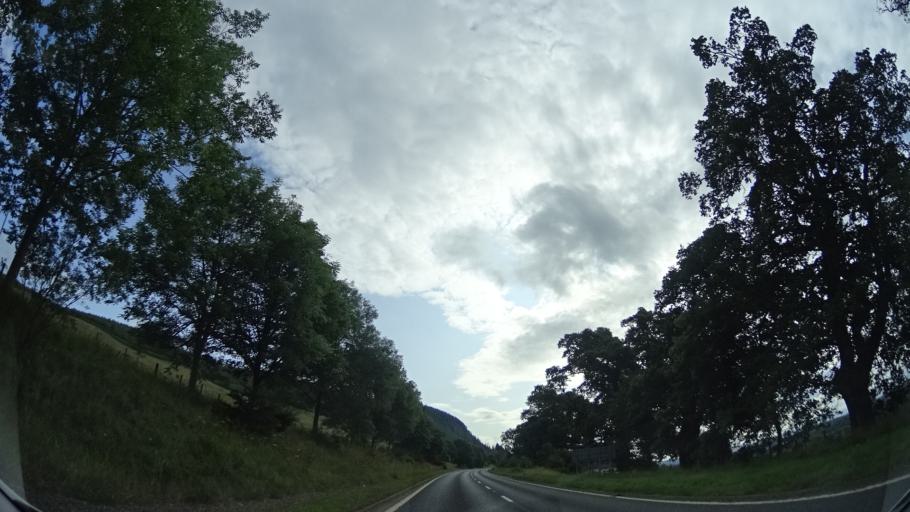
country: GB
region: Scotland
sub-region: Highland
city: Muir of Ord
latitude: 57.5584
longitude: -4.5327
